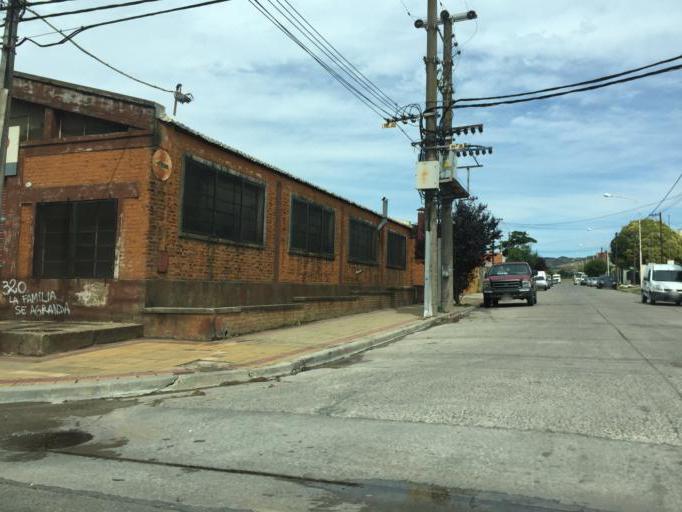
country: AR
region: Buenos Aires
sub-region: Partido de Tandil
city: Tandil
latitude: -37.3239
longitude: -59.1106
